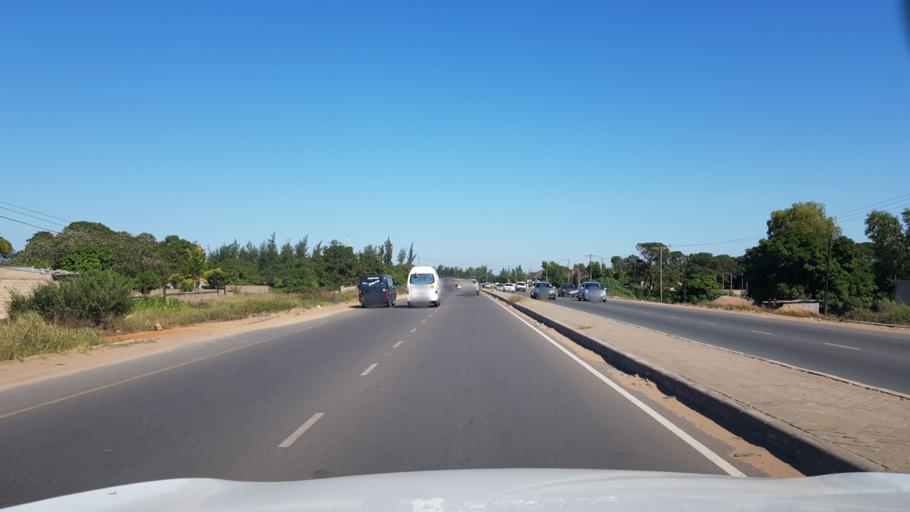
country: MZ
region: Maputo City
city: Maputo
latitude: -25.7995
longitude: 32.5769
